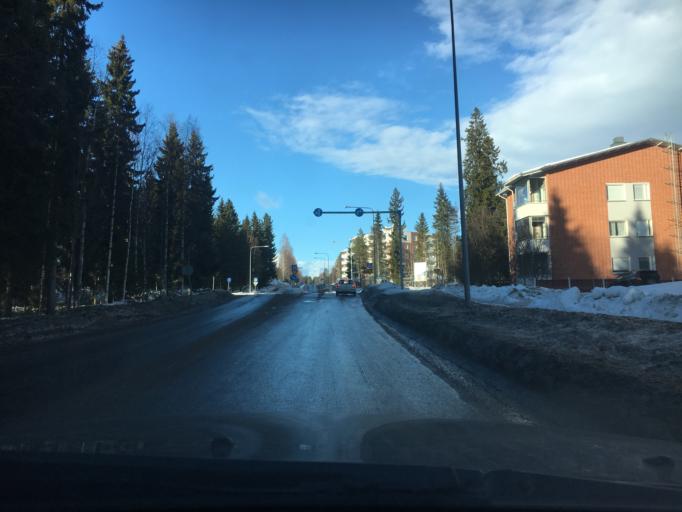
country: FI
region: Kainuu
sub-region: Kajaani
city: Kajaani
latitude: 64.2291
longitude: 27.7525
